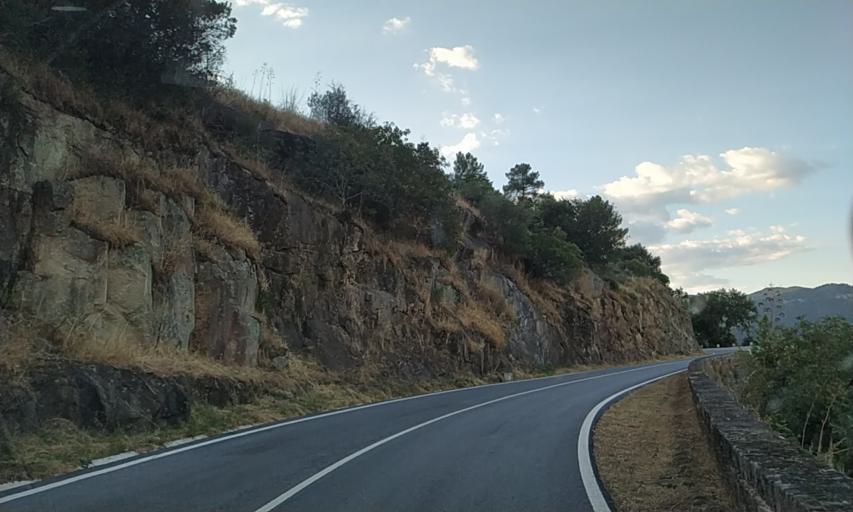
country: PT
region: Viseu
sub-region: Sao Joao da Pesqueira
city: Sao Joao da Pesqueira
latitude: 41.2259
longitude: -7.4240
